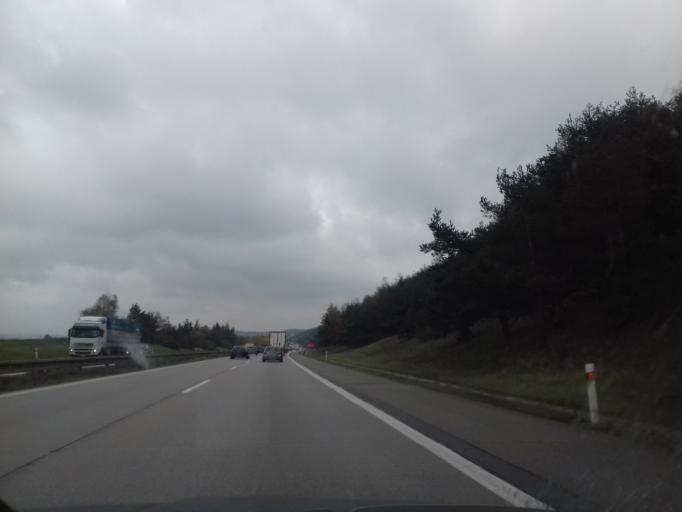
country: CZ
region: Vysocina
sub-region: Okres Zd'ar nad Sazavou
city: Velke Mezirici
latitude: 49.3370
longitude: 16.0590
